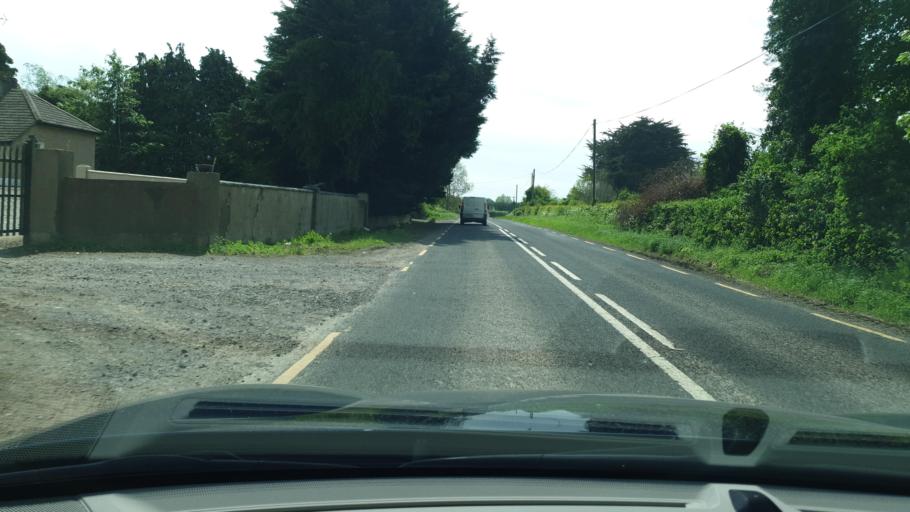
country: IE
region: Leinster
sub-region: An Mhi
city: Navan
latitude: 53.7802
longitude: -6.7280
